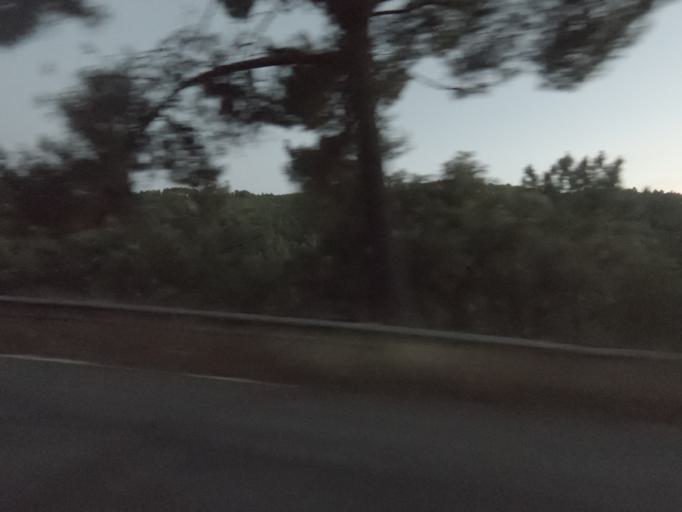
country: PT
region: Vila Real
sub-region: Sabrosa
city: Vilela
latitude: 41.2455
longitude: -7.6830
